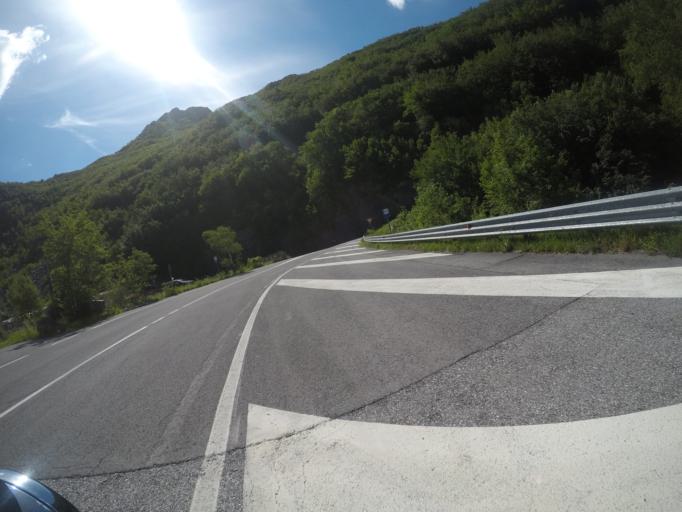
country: IT
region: Tuscany
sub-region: Provincia di Lucca
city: Fontana delle Monache
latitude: 44.0567
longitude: 10.2703
